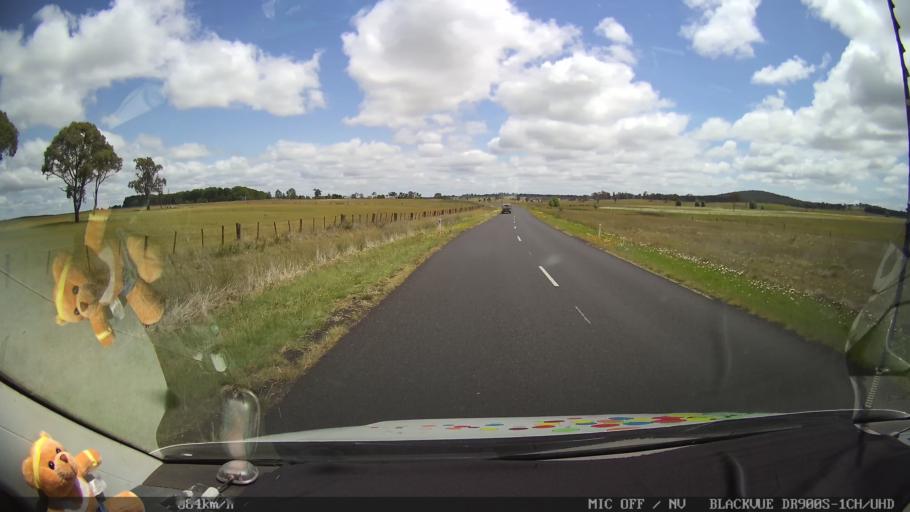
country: AU
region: New South Wales
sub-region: Glen Innes Severn
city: Glen Innes
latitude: -29.6800
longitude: 151.6985
